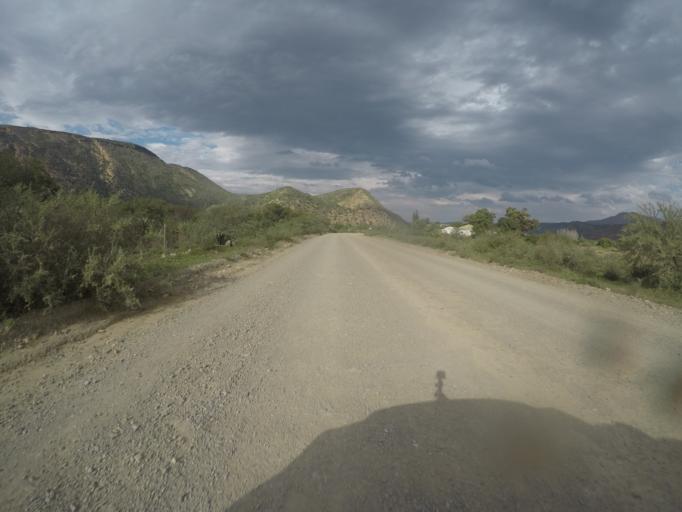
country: ZA
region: Eastern Cape
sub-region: Cacadu District Municipality
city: Kareedouw
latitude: -33.5441
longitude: 23.9820
